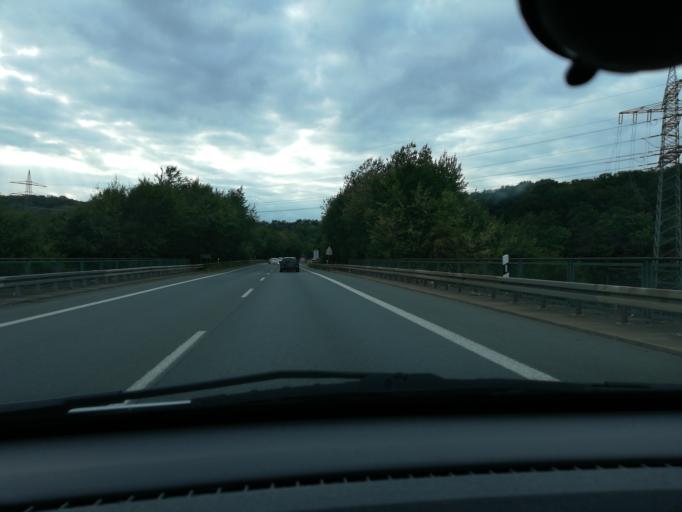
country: DE
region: North Rhine-Westphalia
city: Gevelsberg
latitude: 51.3319
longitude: 7.3660
